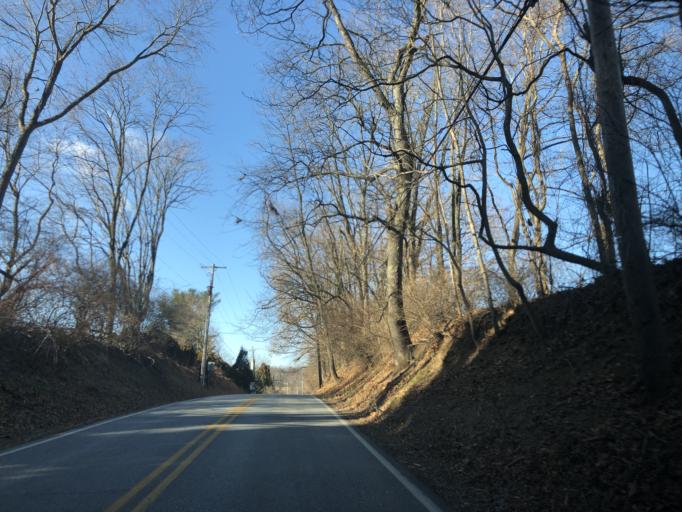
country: US
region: Pennsylvania
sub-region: Chester County
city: Upland
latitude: 39.8962
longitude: -75.7406
